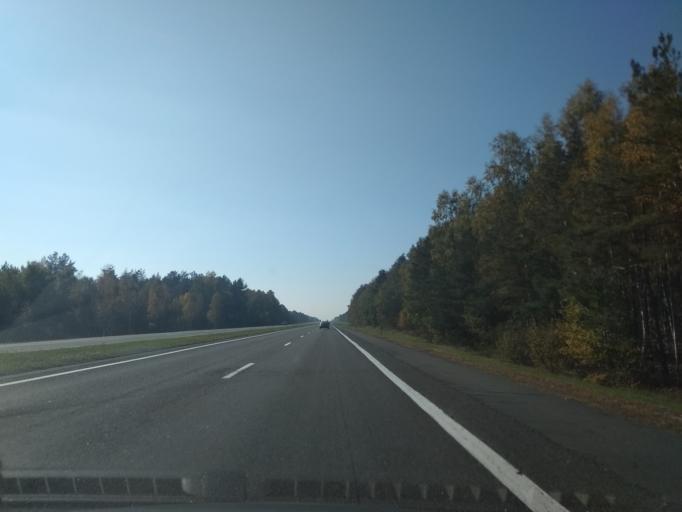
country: BY
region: Brest
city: Ivatsevichy
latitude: 52.7662
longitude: 25.5299
